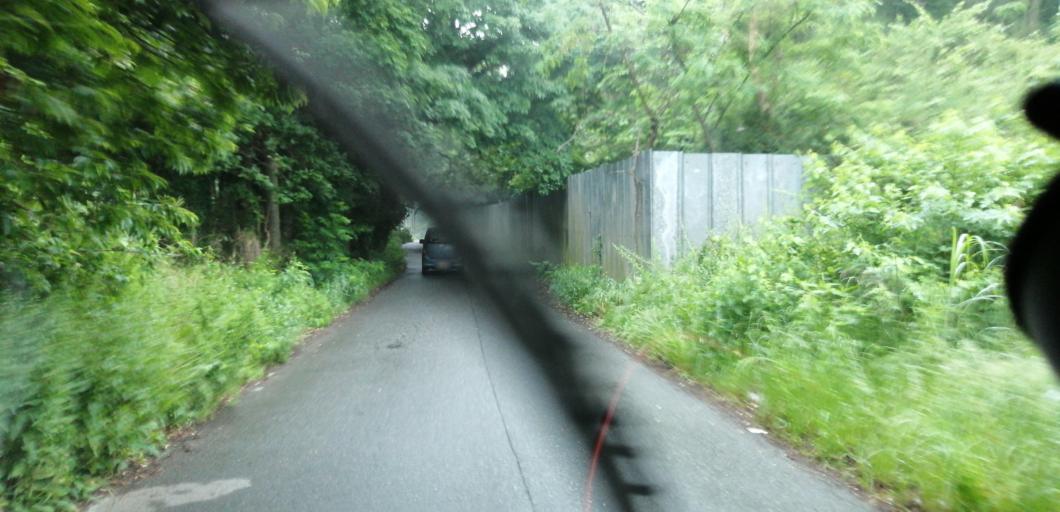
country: JP
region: Chiba
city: Ichihara
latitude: 35.4768
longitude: 140.1503
